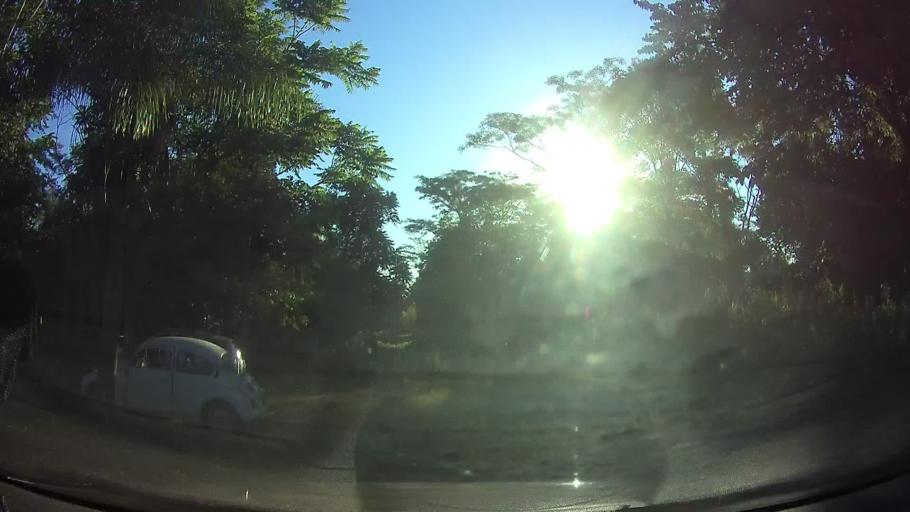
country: PY
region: Central
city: Aregua
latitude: -25.3317
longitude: -57.3971
